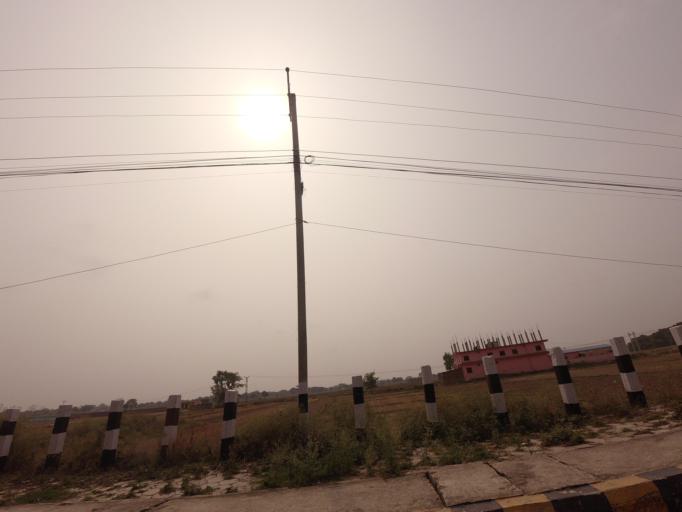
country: IN
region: Uttar Pradesh
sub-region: Maharajganj
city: Nautanwa
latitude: 27.4630
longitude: 83.2837
